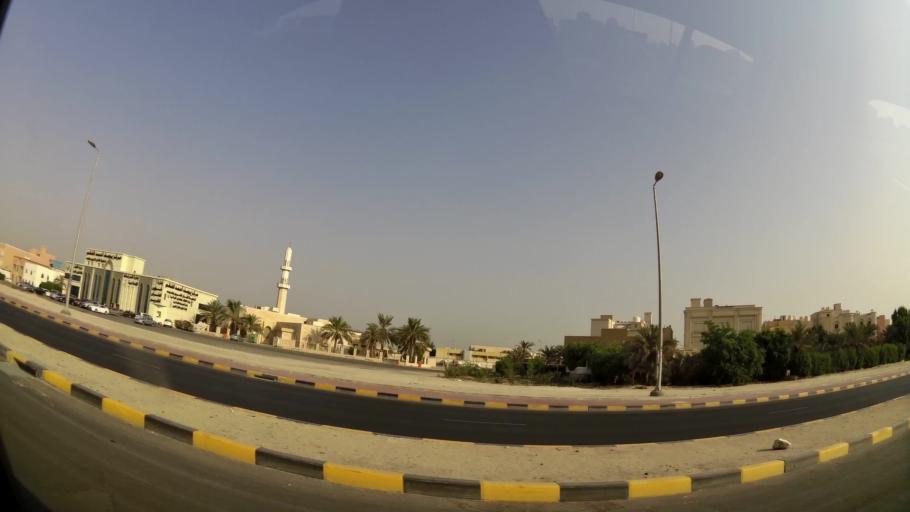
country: KW
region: Al Asimah
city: Ar Rabiyah
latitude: 29.3110
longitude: 47.8555
